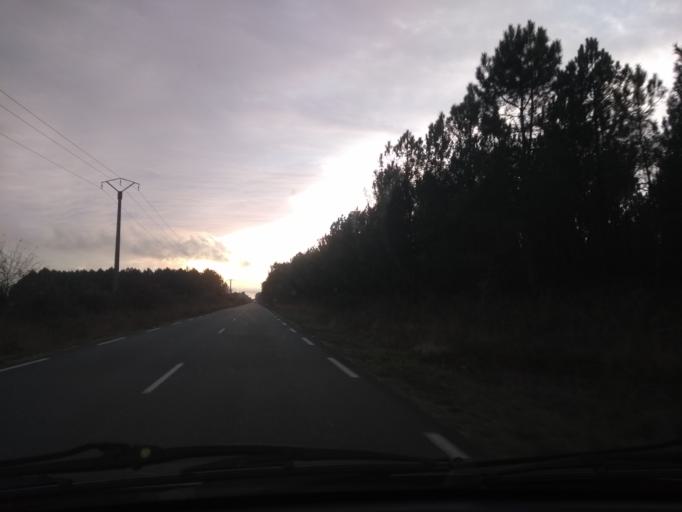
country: FR
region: Aquitaine
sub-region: Departement de la Gironde
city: Le Barp
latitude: 44.6144
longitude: -0.6816
